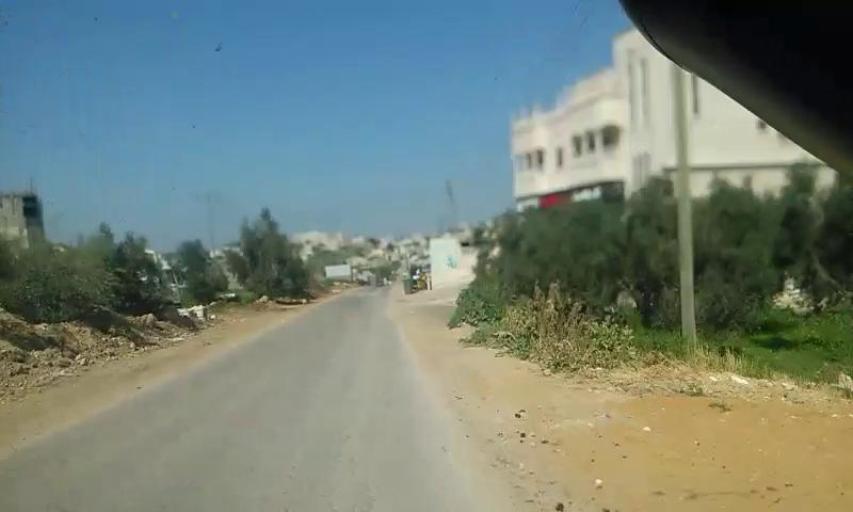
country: PS
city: Dayr Samit
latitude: 31.5102
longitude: 34.9702
